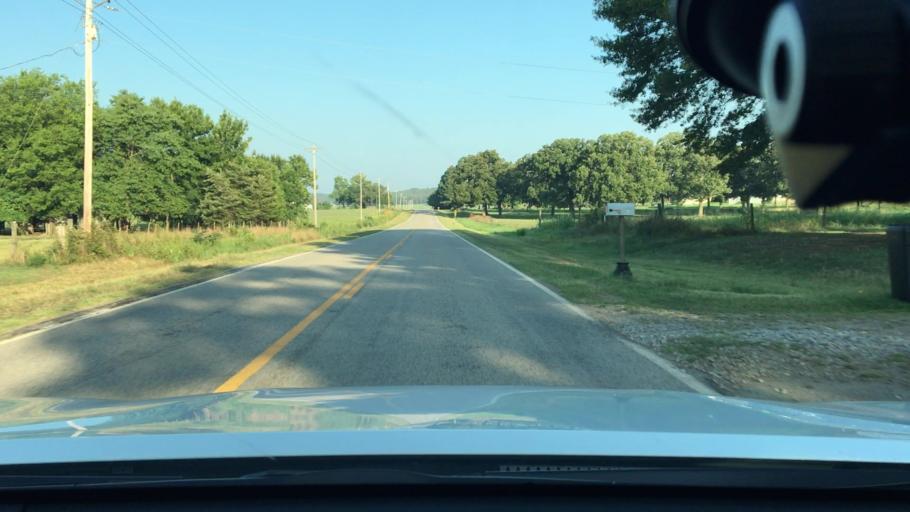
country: US
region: Arkansas
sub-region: Johnson County
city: Coal Hill
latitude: 35.3508
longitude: -93.5757
